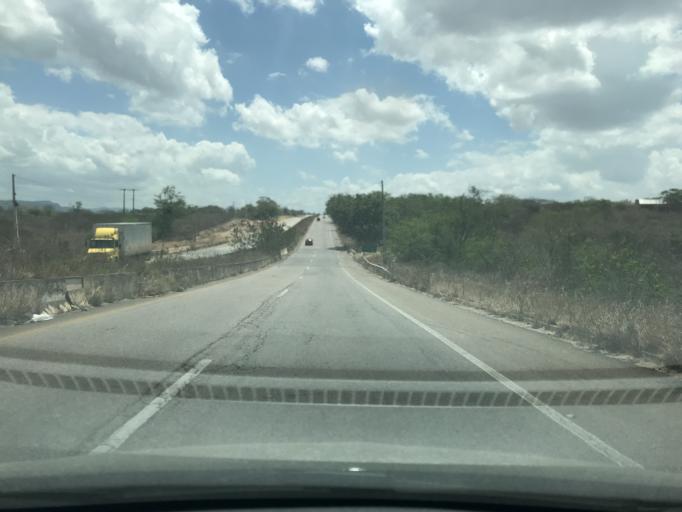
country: BR
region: Pernambuco
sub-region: Caruaru
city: Caruaru
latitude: -8.3002
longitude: -35.9104
